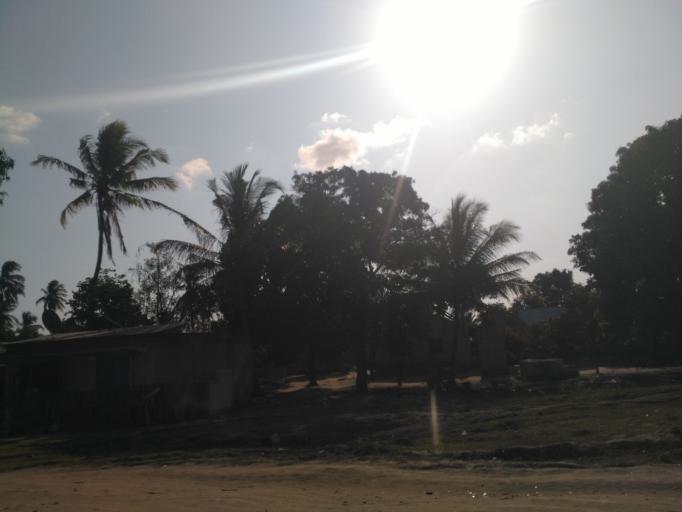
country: TZ
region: Dar es Salaam
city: Dar es Salaam
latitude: -6.8489
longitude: 39.3164
